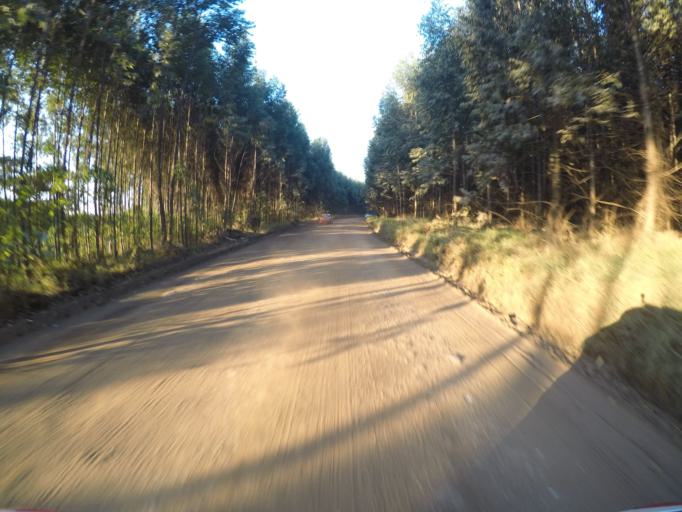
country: ZA
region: KwaZulu-Natal
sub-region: uThungulu District Municipality
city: KwaMbonambi
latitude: -28.6735
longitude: 32.1078
